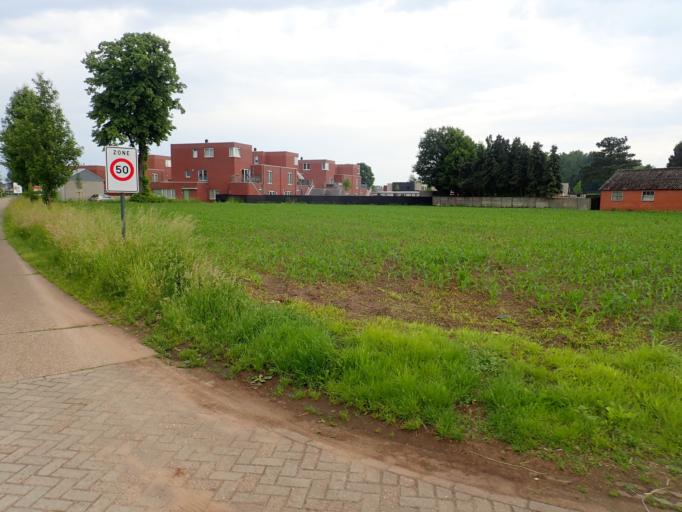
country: BE
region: Flanders
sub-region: Provincie Antwerpen
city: Lille
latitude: 51.2475
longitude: 4.8841
